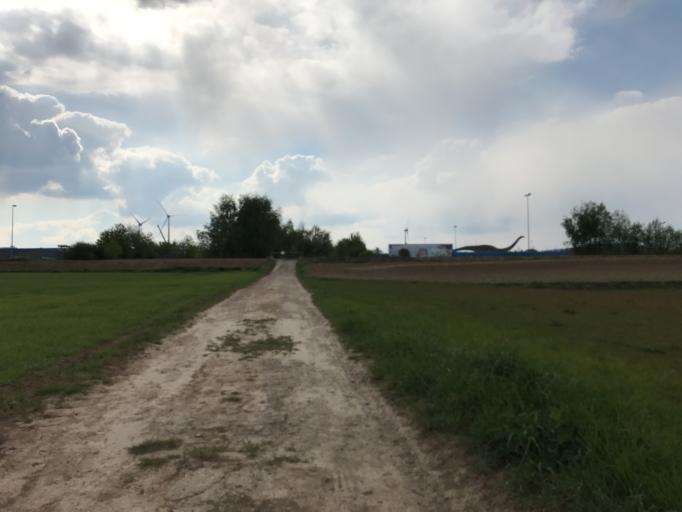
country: DE
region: Rheinland-Pfalz
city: Gau-Bischofsheim
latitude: 49.9429
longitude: 8.2586
